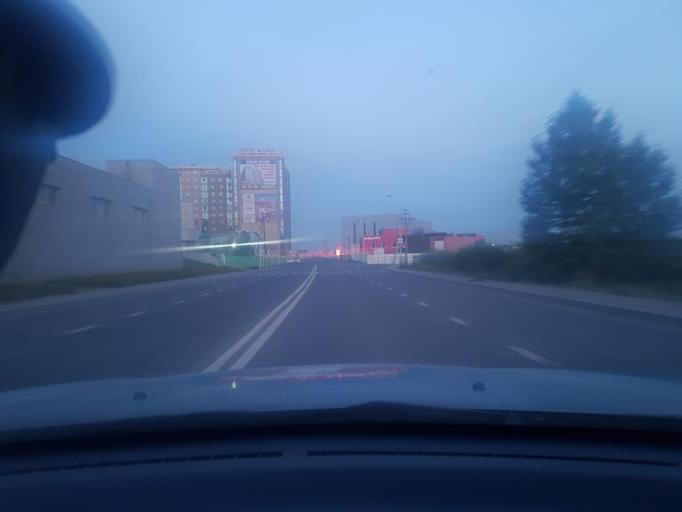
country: MN
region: Ulaanbaatar
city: Ulaanbaatar
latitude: 47.9036
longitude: 106.8787
